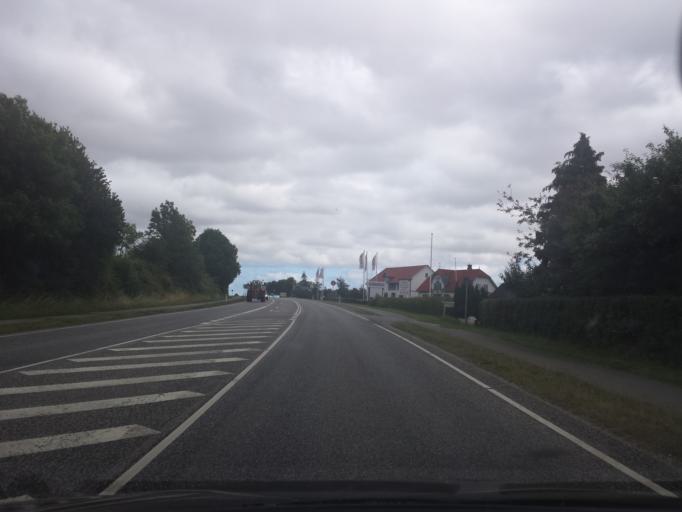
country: DK
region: South Denmark
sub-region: Sonderborg Kommune
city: Guderup
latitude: 54.9866
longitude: 9.8644
